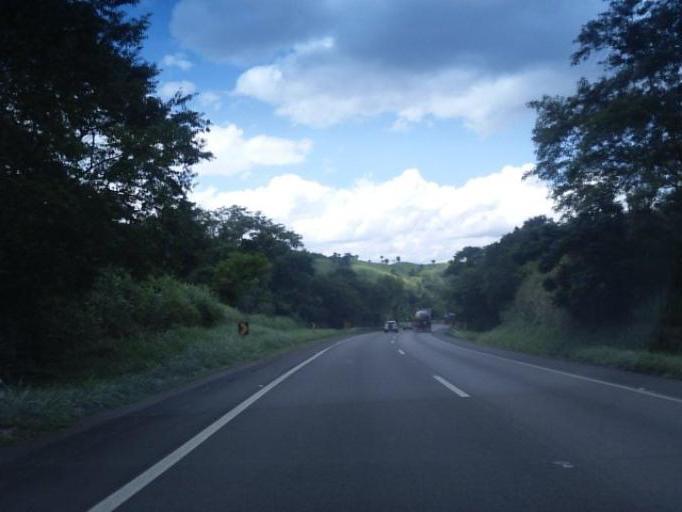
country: BR
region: Sao Paulo
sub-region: Cajati
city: Cajati
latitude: -24.7791
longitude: -48.2010
